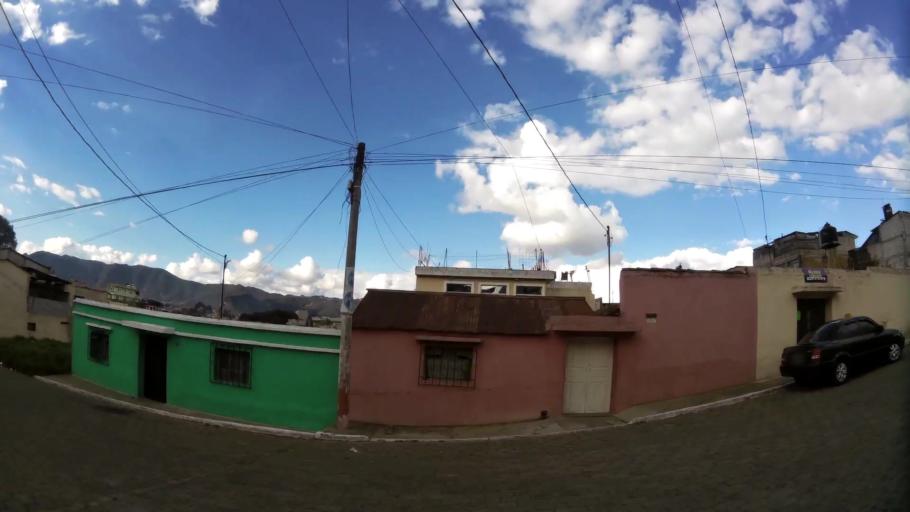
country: GT
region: Quetzaltenango
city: Quetzaltenango
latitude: 14.8486
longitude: -91.5191
